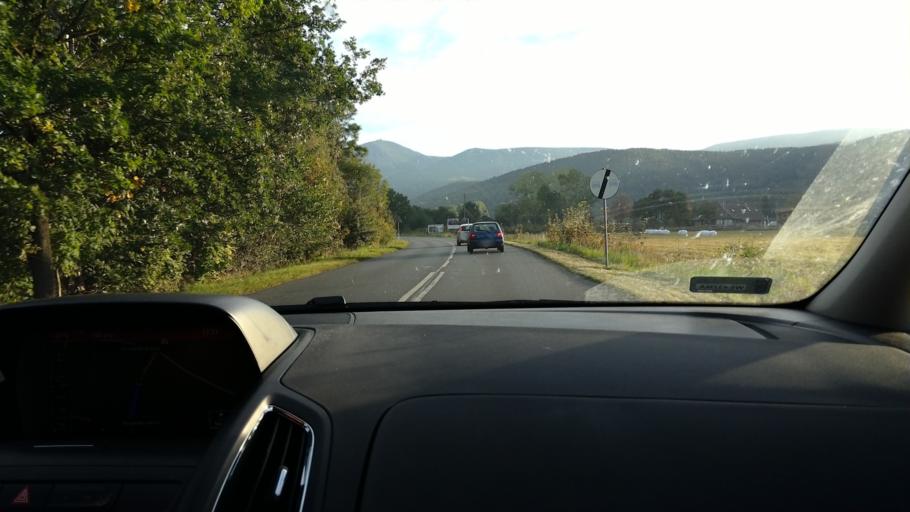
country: PL
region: Lower Silesian Voivodeship
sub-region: Powiat jeleniogorski
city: Myslakowice
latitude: 50.8095
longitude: 15.7669
